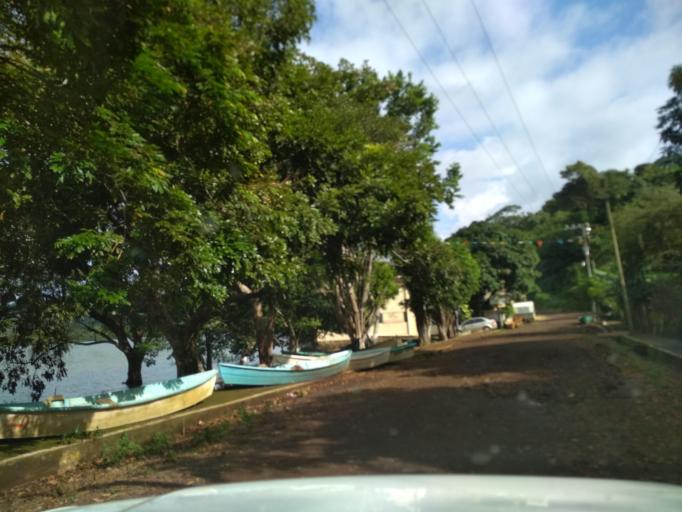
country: MX
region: Veracruz
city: Catemaco
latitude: 18.3726
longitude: -95.1169
